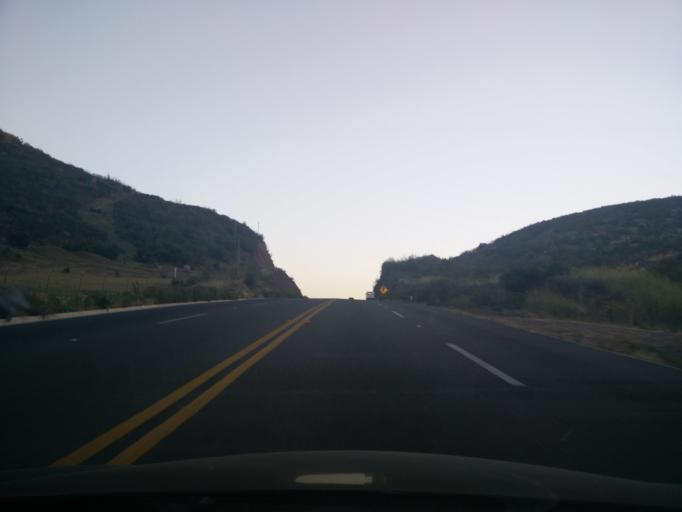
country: MX
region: Baja California
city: El Sauzal
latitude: 31.9413
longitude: -116.6695
